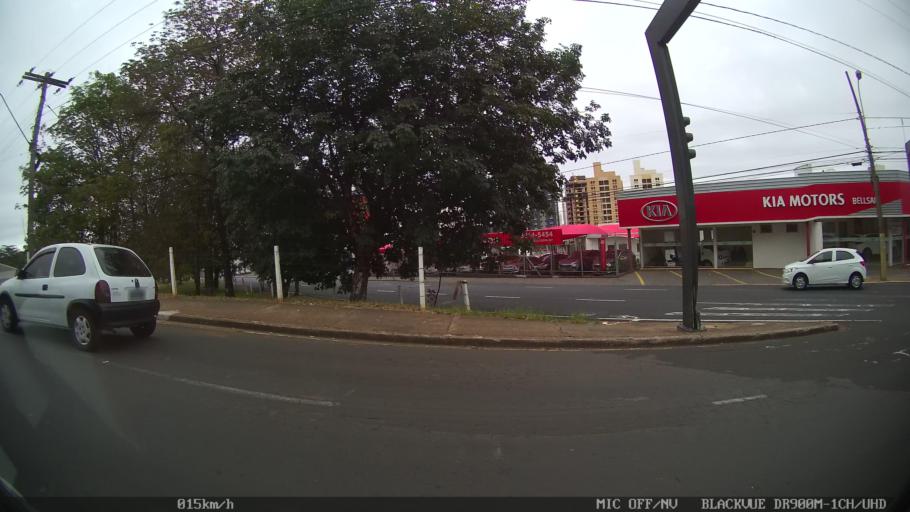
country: BR
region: Sao Paulo
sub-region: Sao Jose Do Rio Preto
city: Sao Jose do Rio Preto
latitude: -20.8228
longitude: -49.3944
